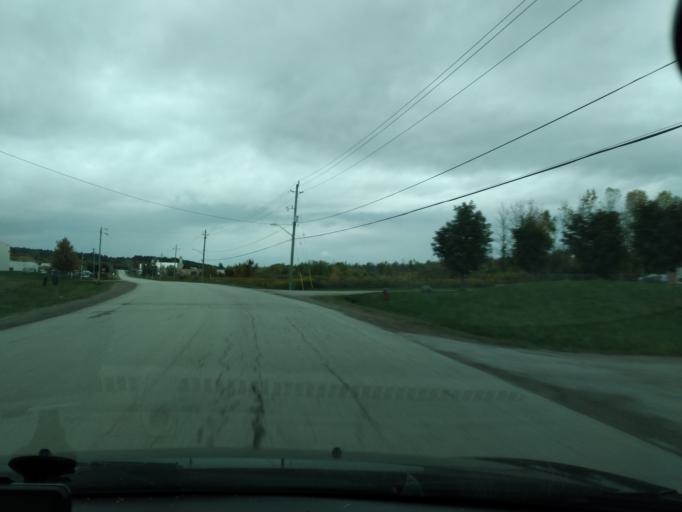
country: CA
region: Ontario
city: Bradford West Gwillimbury
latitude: 44.1324
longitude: -79.5554
